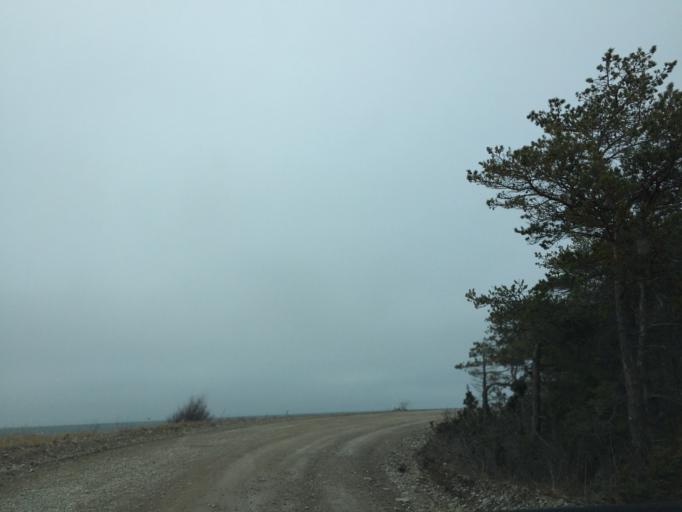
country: EE
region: Saare
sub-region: Kuressaare linn
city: Kuressaare
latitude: 58.5033
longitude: 21.9112
